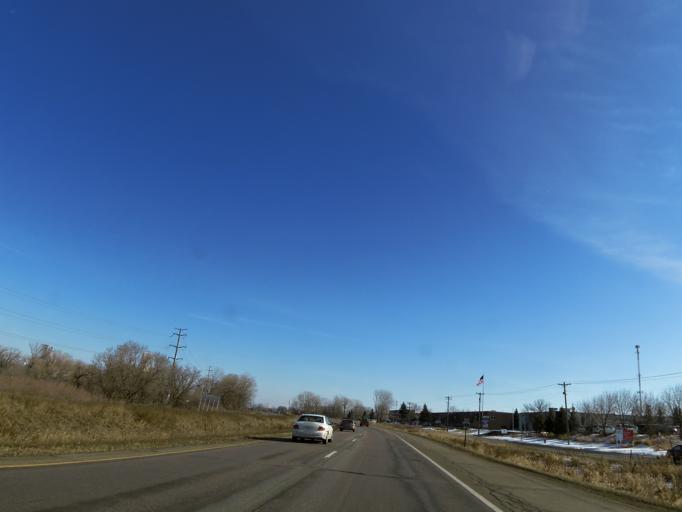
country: US
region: Minnesota
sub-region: Scott County
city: Savage
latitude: 44.7775
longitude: -93.3660
